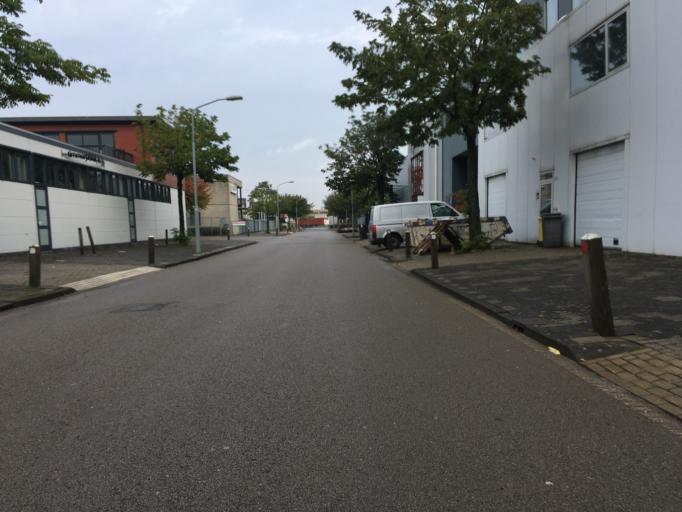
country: NL
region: North Holland
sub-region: Gemeente Haarlem
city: Haarlem
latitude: 52.3893
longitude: 4.6676
